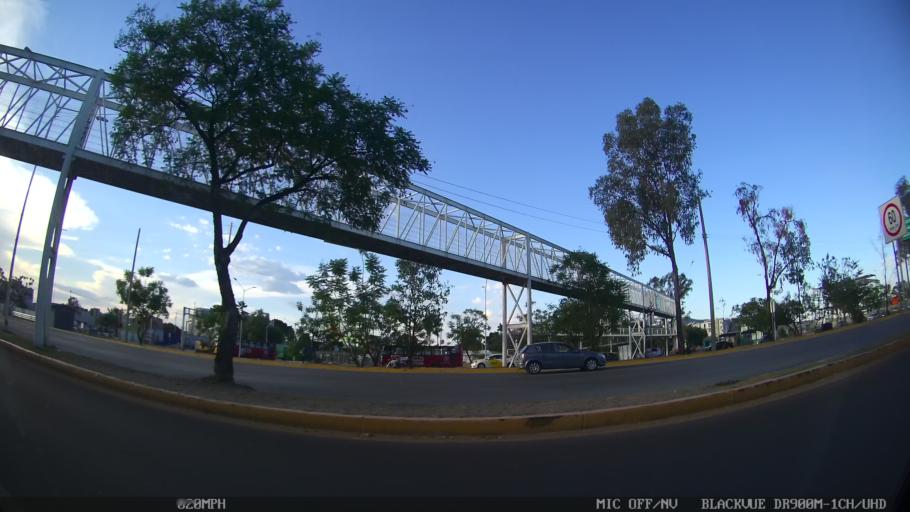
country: MX
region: Jalisco
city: Tlaquepaque
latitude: 20.7138
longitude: -103.3011
